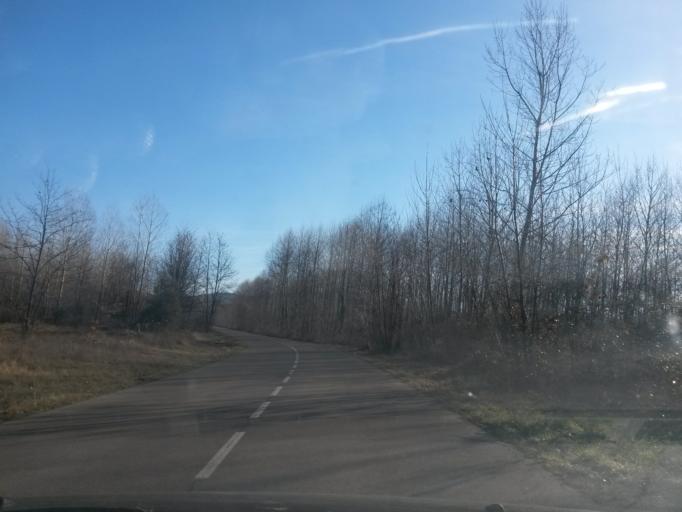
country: ES
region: Catalonia
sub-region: Provincia de Girona
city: Angles
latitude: 41.9634
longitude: 2.6532
